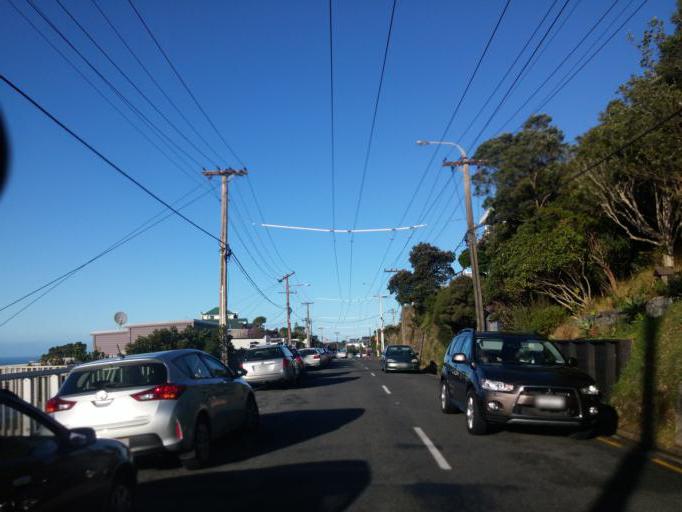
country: NZ
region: Wellington
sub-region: Wellington City
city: Brooklyn
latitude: -41.3147
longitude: 174.7655
